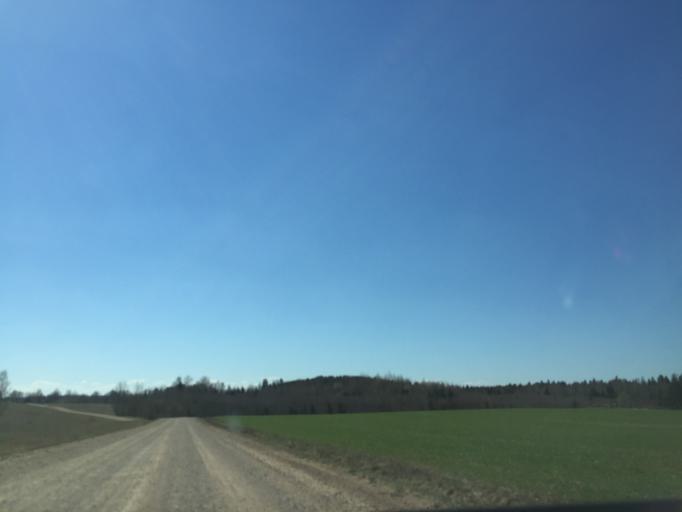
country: EE
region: Viljandimaa
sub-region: Viiratsi vald
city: Viiratsi
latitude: 58.3365
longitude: 25.7126
